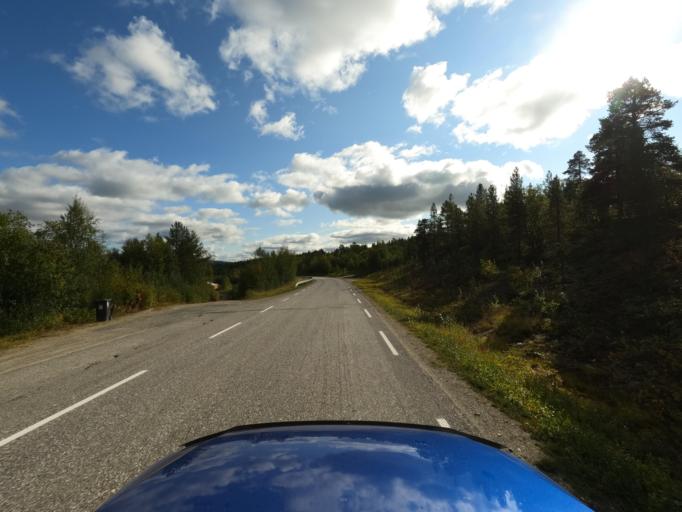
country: NO
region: Finnmark Fylke
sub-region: Karasjok
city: Karasjohka
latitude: 69.4339
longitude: 25.7141
